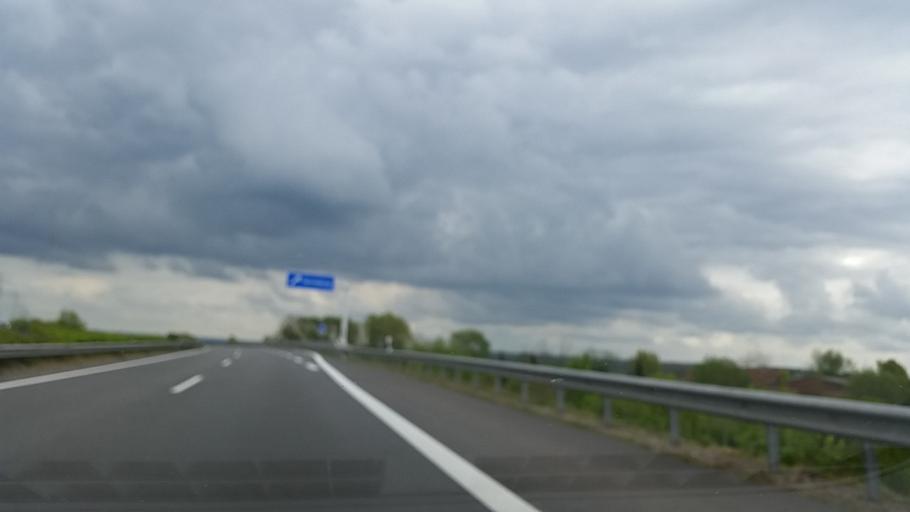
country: DE
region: Lower Saxony
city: Neuenkirchen
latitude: 53.5160
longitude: 9.5911
